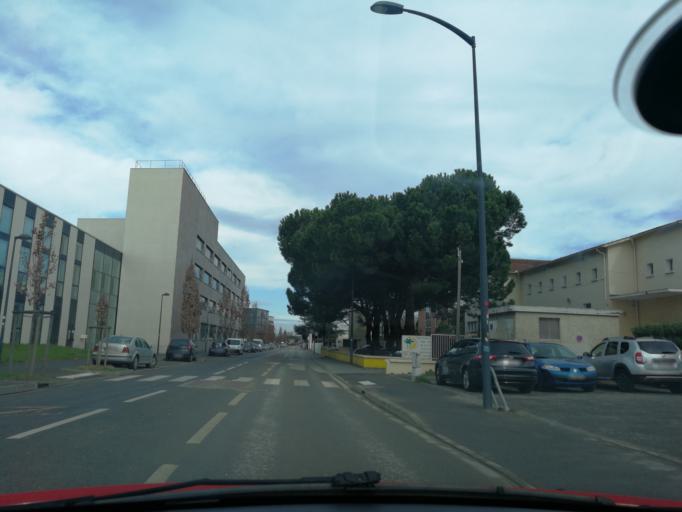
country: FR
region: Midi-Pyrenees
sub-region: Departement de la Haute-Garonne
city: Balma
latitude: 43.6246
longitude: 1.4861
